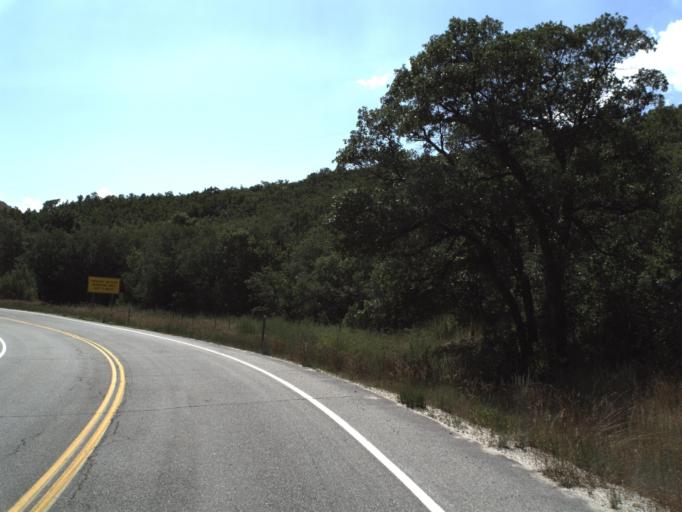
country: US
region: Utah
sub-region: Weber County
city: Wolf Creek
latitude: 41.2689
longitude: -111.6730
